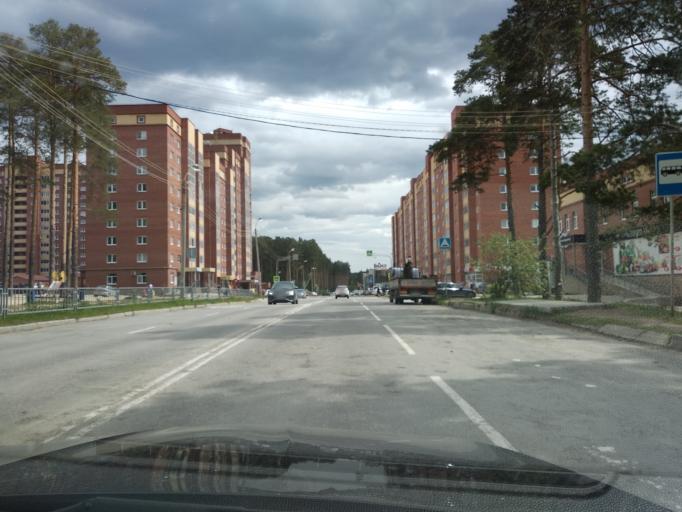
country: RU
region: Sverdlovsk
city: Beryozovsky
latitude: 56.9135
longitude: 60.8195
